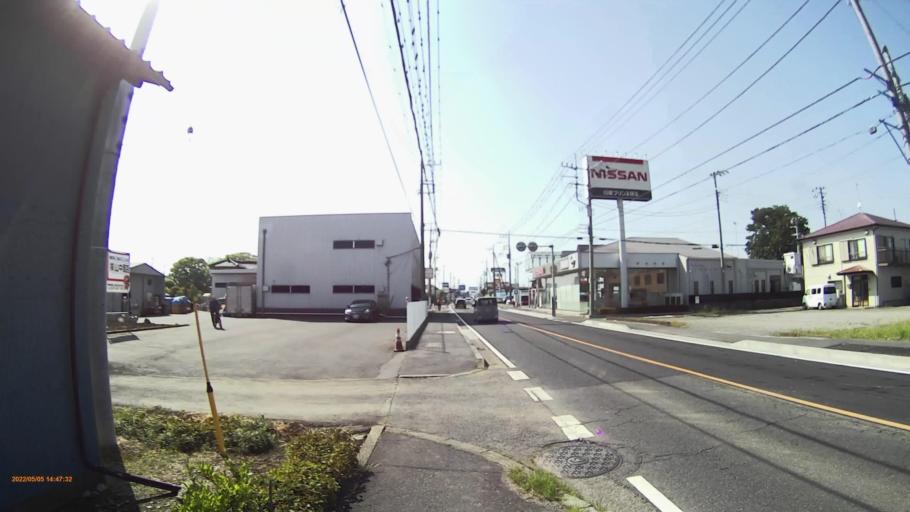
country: JP
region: Saitama
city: Sugito
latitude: 36.0178
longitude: 139.7488
